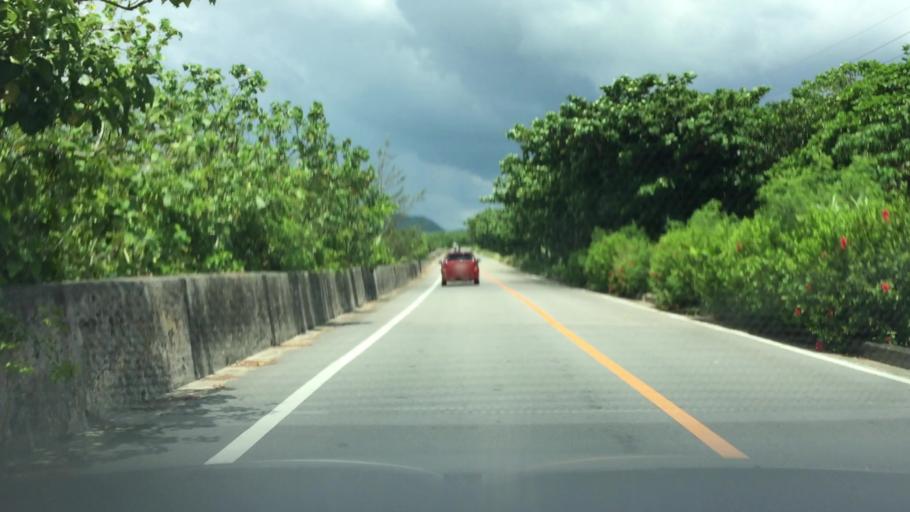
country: JP
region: Okinawa
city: Ishigaki
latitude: 24.4260
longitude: 124.1276
